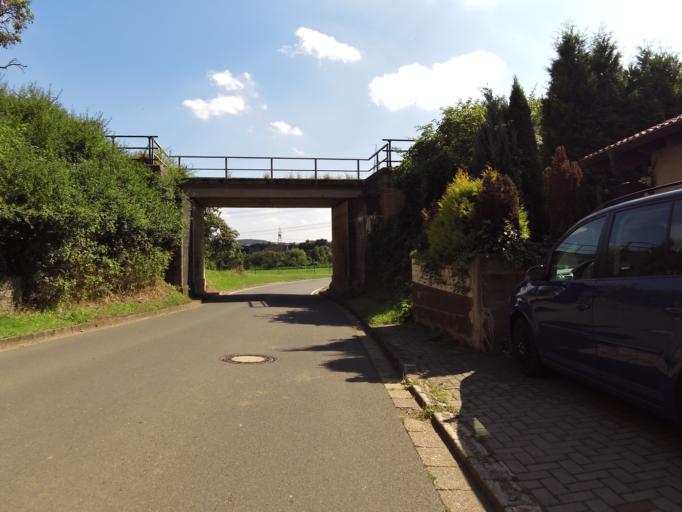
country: DE
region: Rheinland-Pfalz
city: Borrstadt
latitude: 49.5838
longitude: 7.9430
